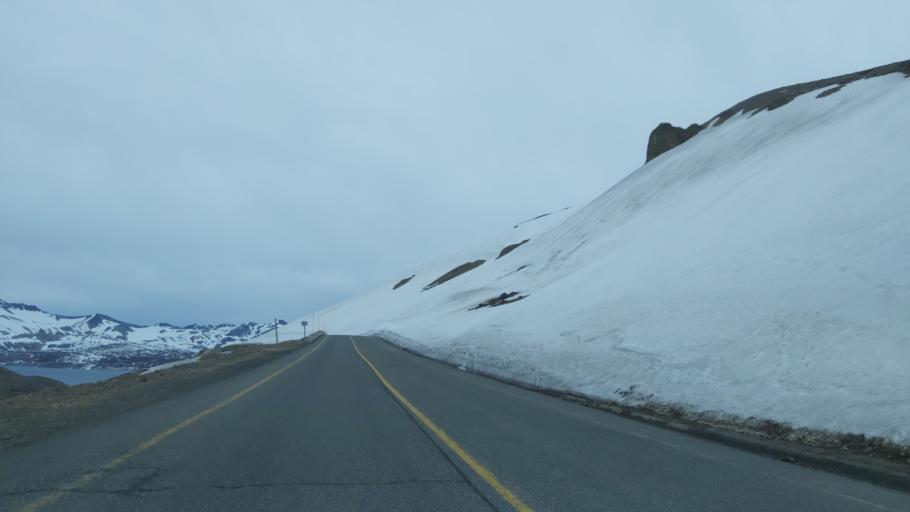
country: CL
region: Maule
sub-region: Provincia de Linares
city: Colbun
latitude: -36.0151
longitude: -70.4967
